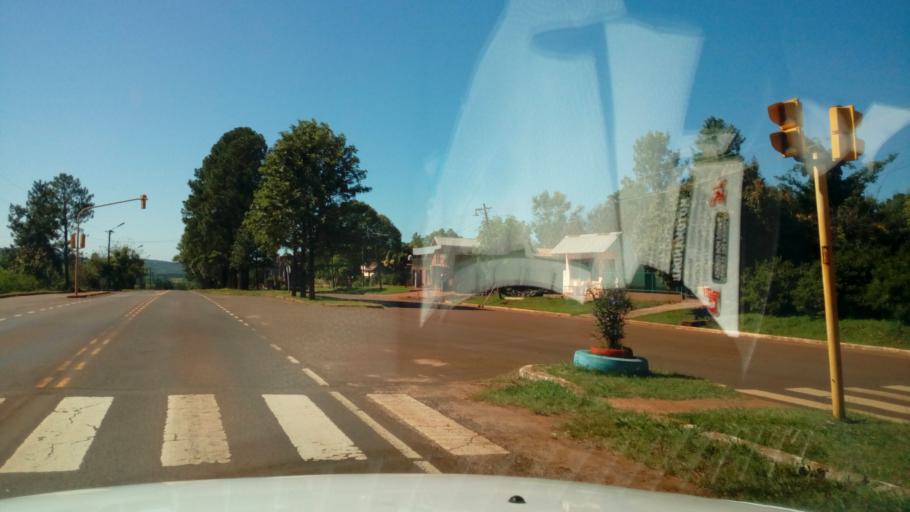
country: AR
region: Misiones
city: Bonpland
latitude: -27.4799
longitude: -55.4745
